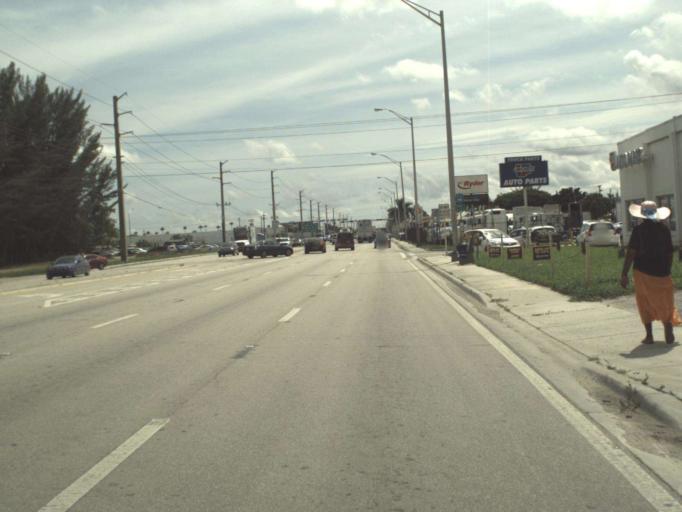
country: US
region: Florida
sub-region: Miami-Dade County
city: Virginia Gardens
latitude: 25.8123
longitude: -80.3135
